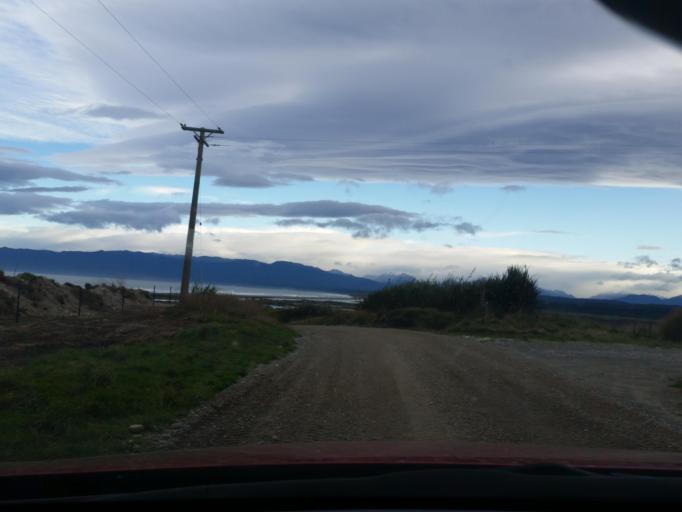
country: NZ
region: Southland
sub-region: Southland District
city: Riverton
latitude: -46.2039
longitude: 167.6388
